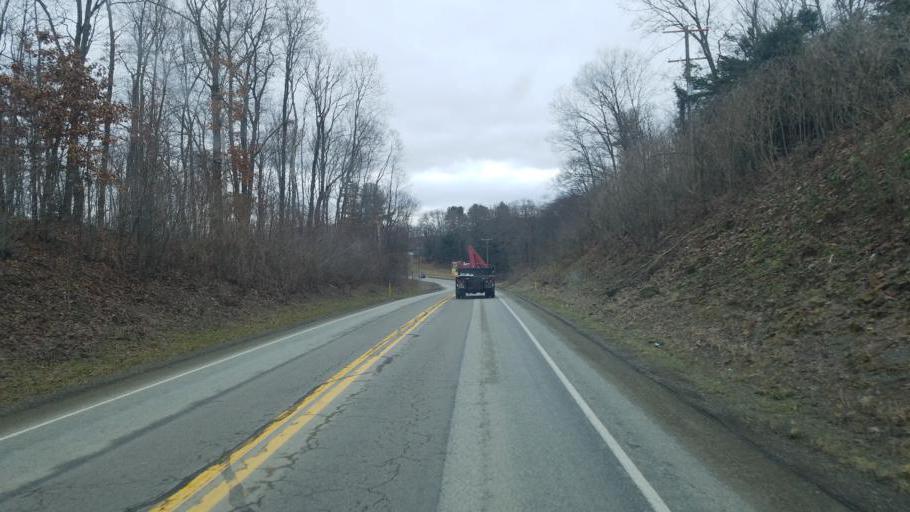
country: US
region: Pennsylvania
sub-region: Clarion County
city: Marianne
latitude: 41.3442
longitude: -79.3426
